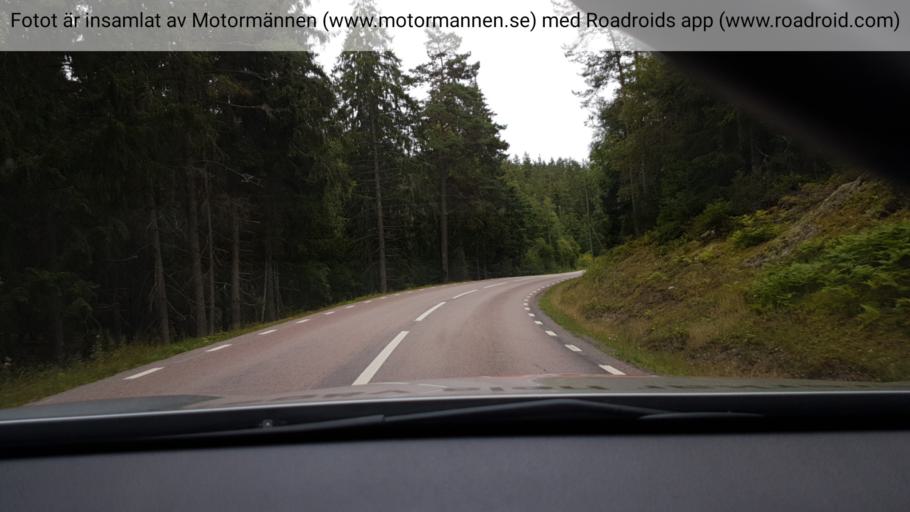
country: SE
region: Soedermanland
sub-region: Nykopings Kommun
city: Nykoping
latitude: 58.8477
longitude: 17.0618
